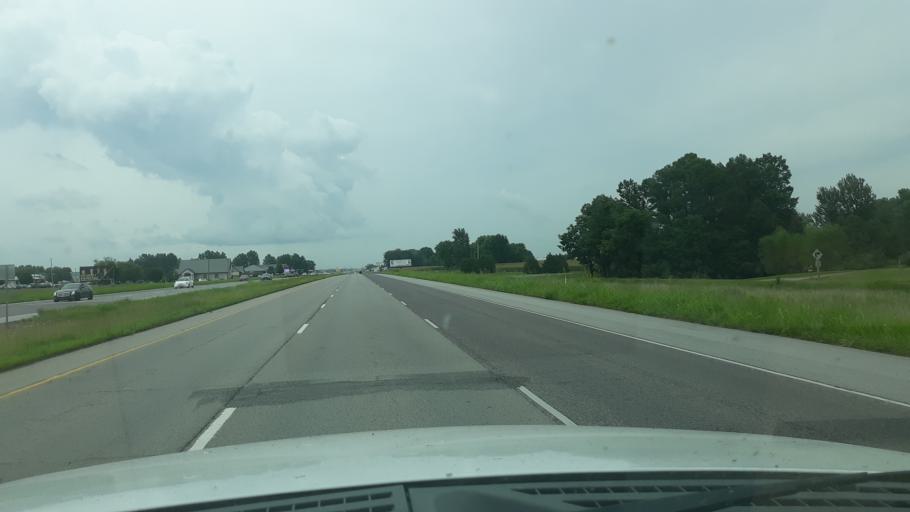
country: US
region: Illinois
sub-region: Williamson County
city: Energy
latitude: 37.7450
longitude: -89.0342
